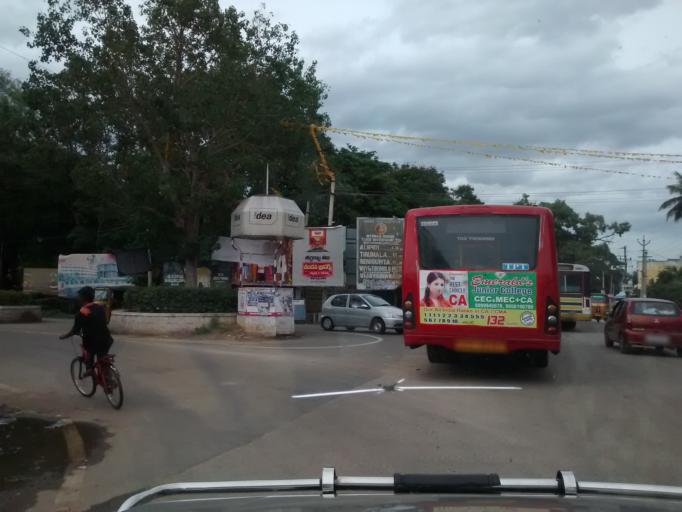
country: IN
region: Andhra Pradesh
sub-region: Chittoor
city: Narasingapuram
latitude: 13.6142
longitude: 79.3633
